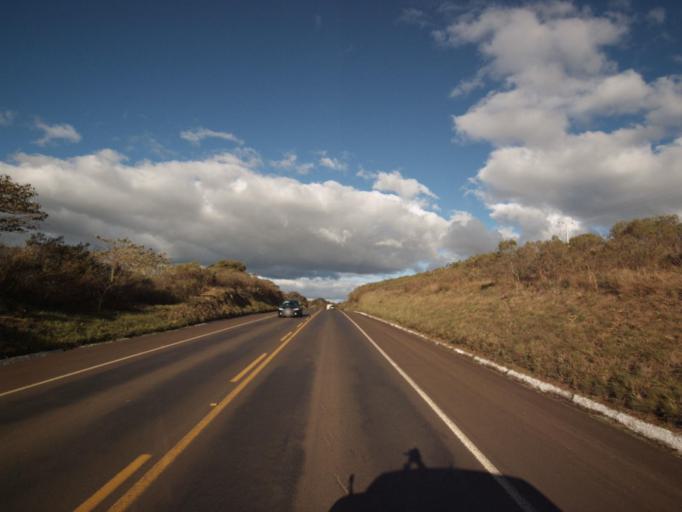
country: BR
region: Santa Catarina
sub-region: Campos Novos
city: Campos Novos
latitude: -27.3620
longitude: -51.3144
